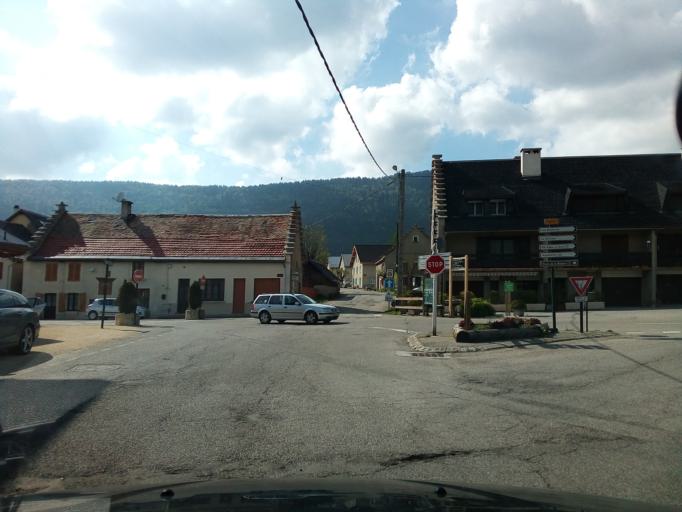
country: FR
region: Rhone-Alpes
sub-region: Departement de l'Isere
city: Autrans
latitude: 45.1761
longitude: 5.5450
